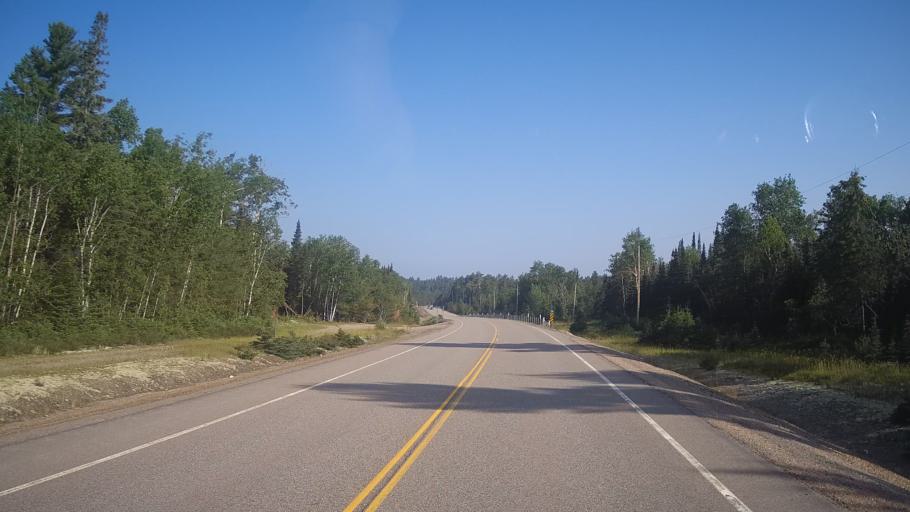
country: CA
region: Ontario
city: Rayside-Balfour
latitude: 46.7376
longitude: -81.5934
